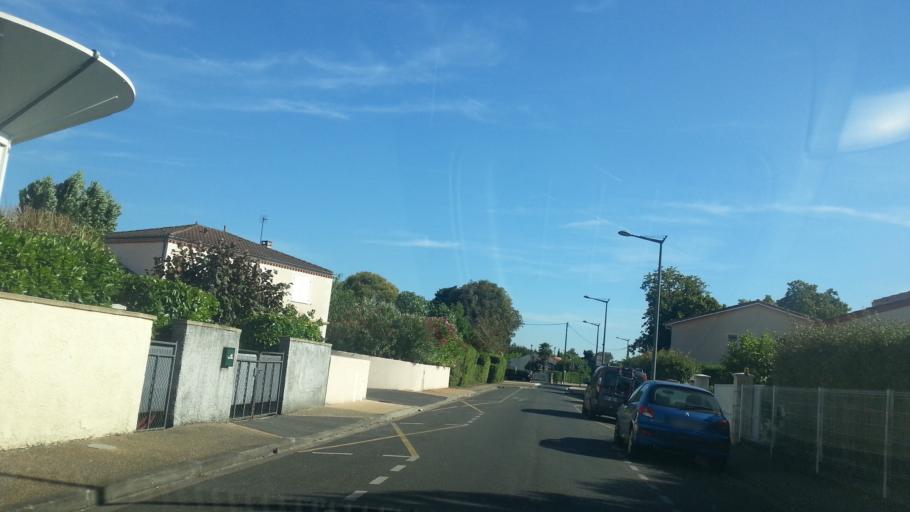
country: FR
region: Aquitaine
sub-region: Departement de la Gironde
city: Bassens
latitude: 44.8981
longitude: -0.5163
